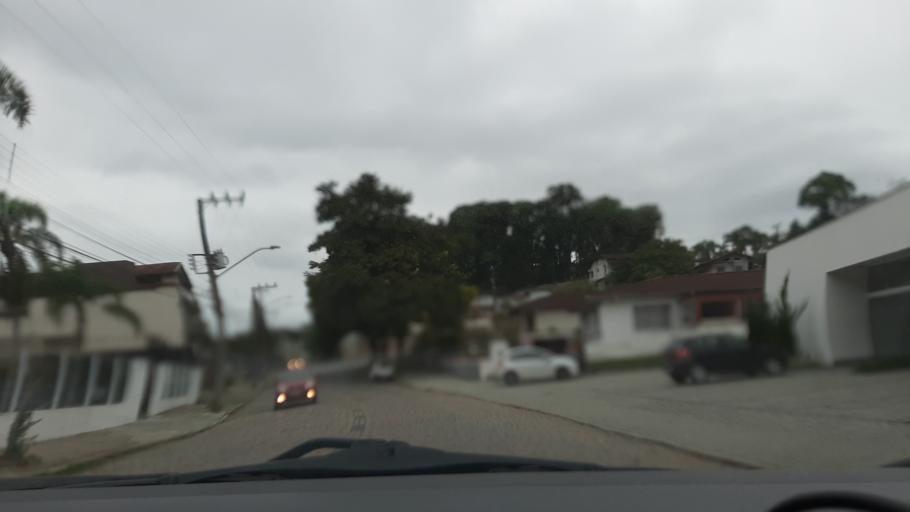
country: BR
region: Santa Catarina
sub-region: Joinville
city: Joinville
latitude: -26.3164
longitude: -48.8578
